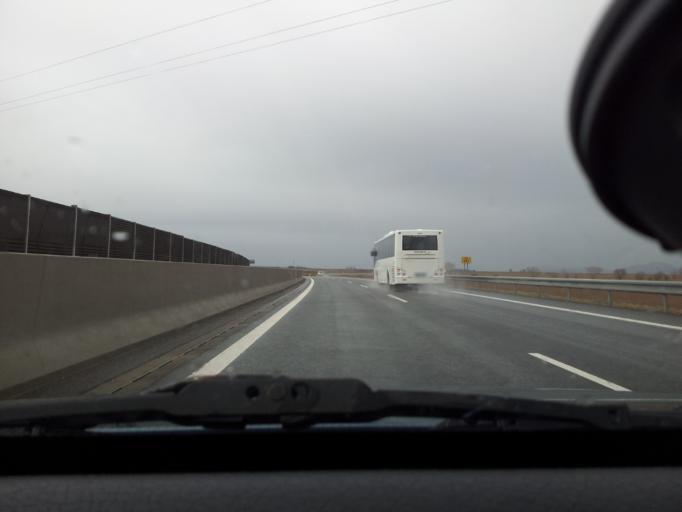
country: SK
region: Nitriansky
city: Zlate Moravce
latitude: 48.3493
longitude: 18.3598
